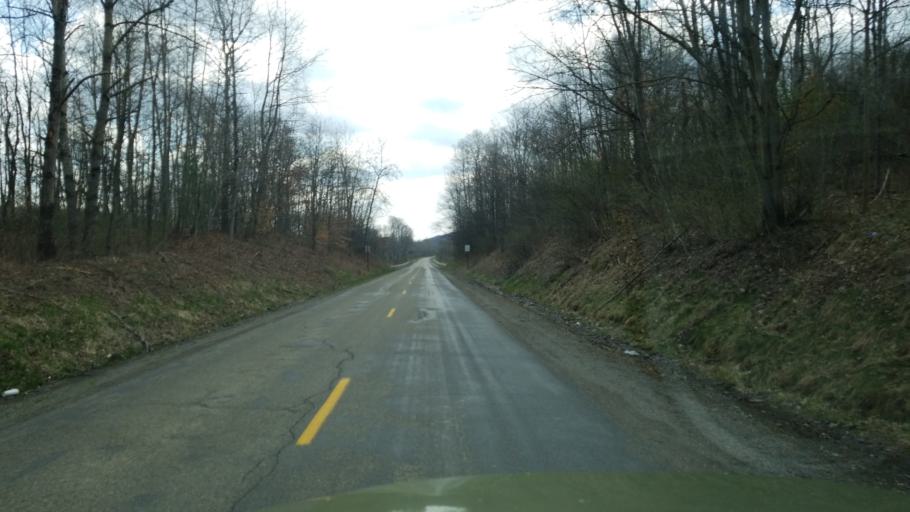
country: US
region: Pennsylvania
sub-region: Jefferson County
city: Brockway
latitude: 41.2626
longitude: -78.8099
